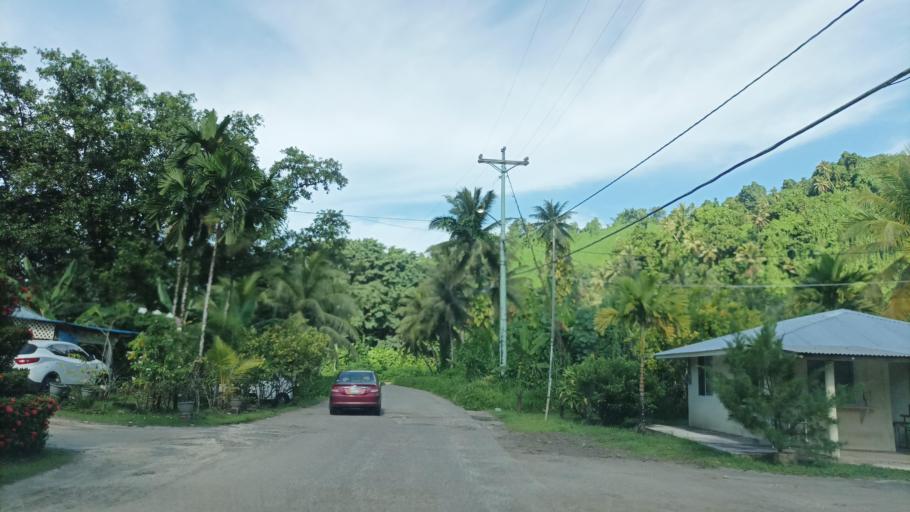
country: FM
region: Kosrae
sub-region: Lelu Municipality
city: Lelu
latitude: 5.3180
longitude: 163.0240
